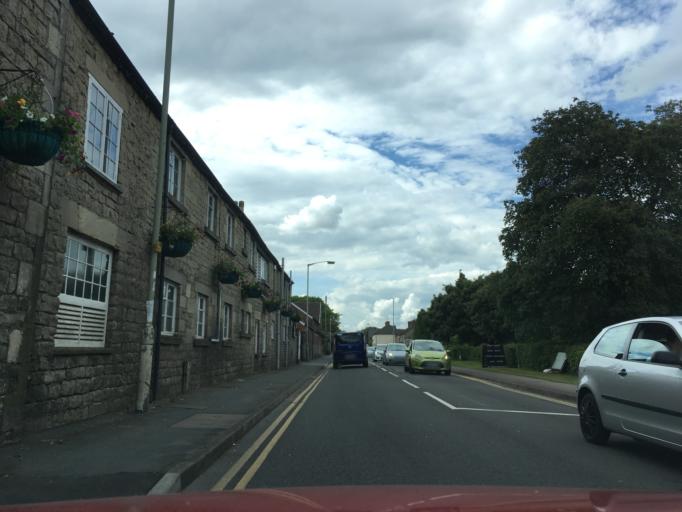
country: GB
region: England
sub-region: Borough of Swindon
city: Broad Blunsdon
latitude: 51.5922
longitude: -1.7618
